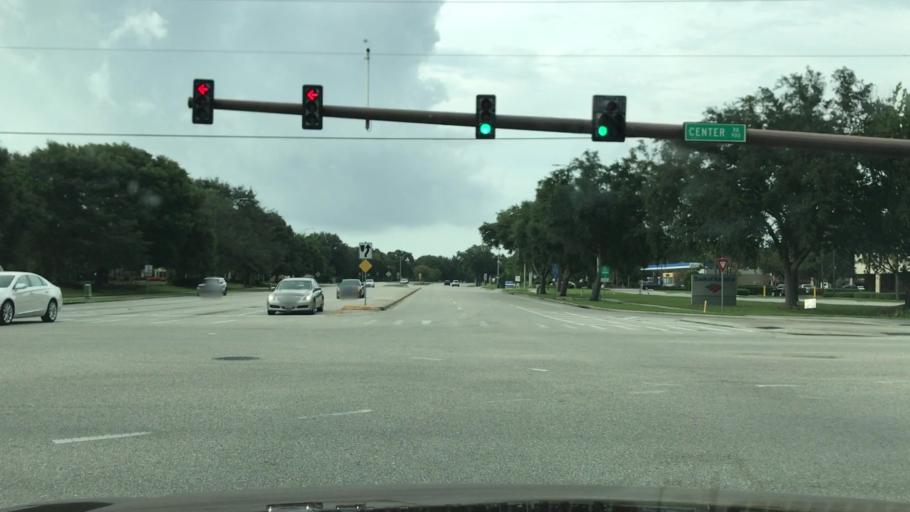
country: US
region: Florida
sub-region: Sarasota County
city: Plantation
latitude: 27.0791
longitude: -82.3888
